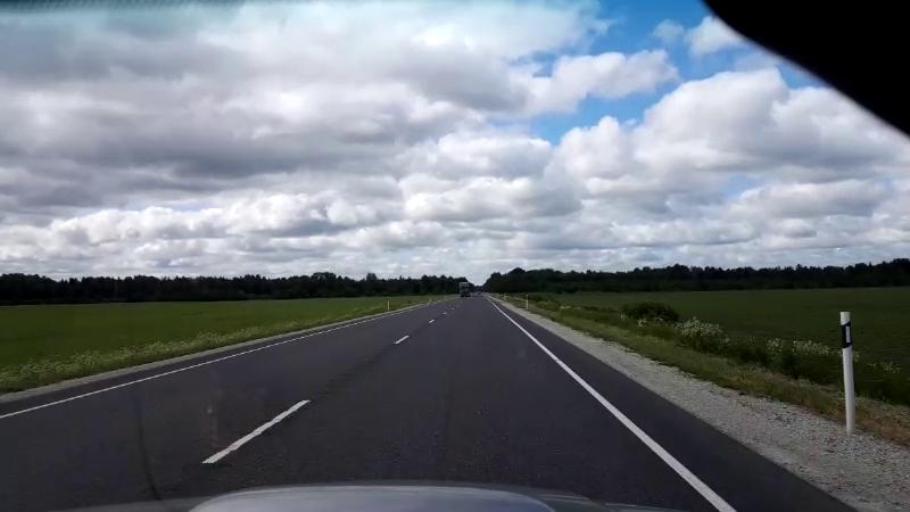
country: EE
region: Raplamaa
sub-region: Maerjamaa vald
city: Marjamaa
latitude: 58.8449
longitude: 24.4266
